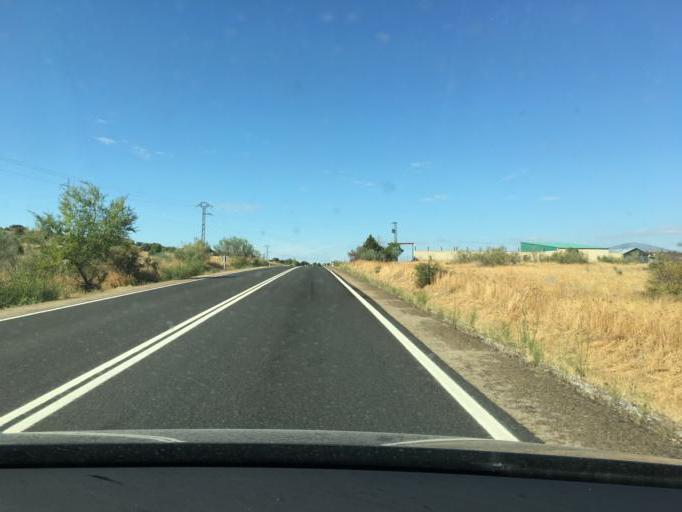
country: ES
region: Madrid
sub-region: Provincia de Madrid
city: Reduena
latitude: 40.8142
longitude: -3.5845
